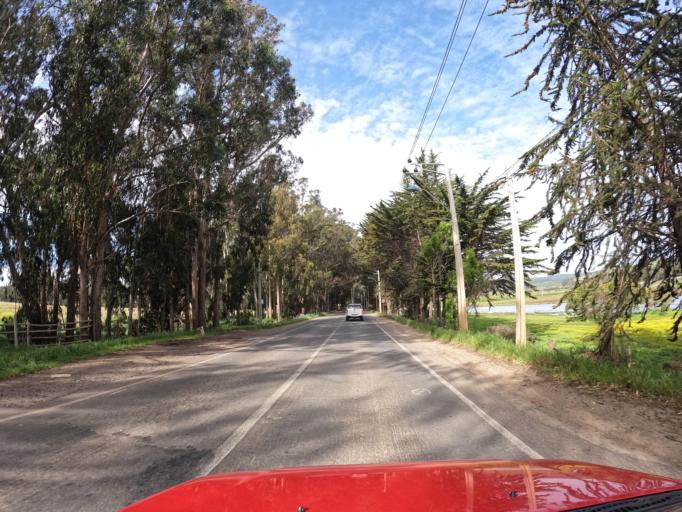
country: CL
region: O'Higgins
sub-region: Provincia de Colchagua
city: Santa Cruz
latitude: -34.3851
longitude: -71.9852
